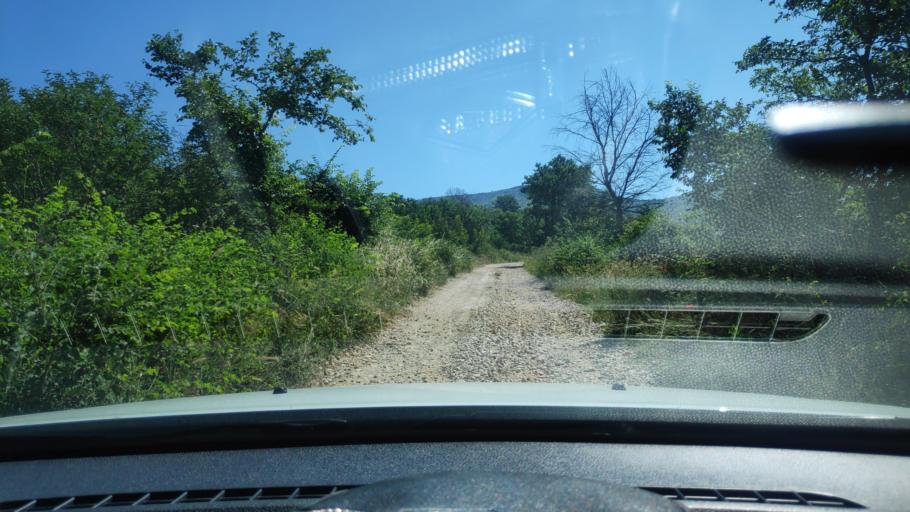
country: MK
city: Klechovce
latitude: 42.0710
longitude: 21.8858
